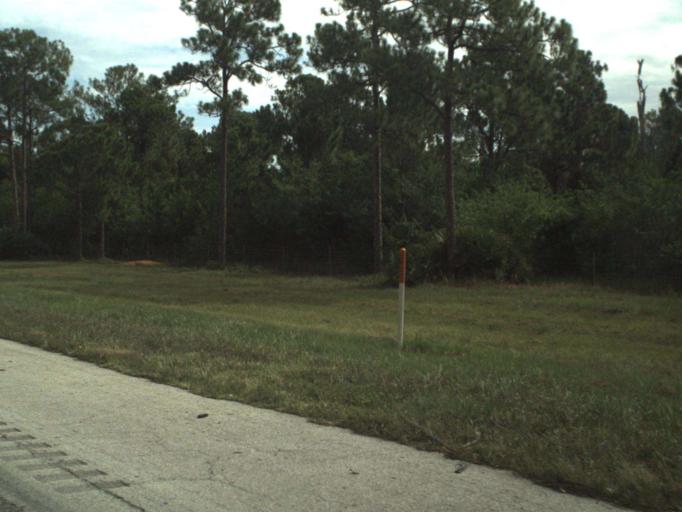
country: US
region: Florida
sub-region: Saint Lucie County
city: Port Saint Lucie
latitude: 27.1740
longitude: -80.3944
